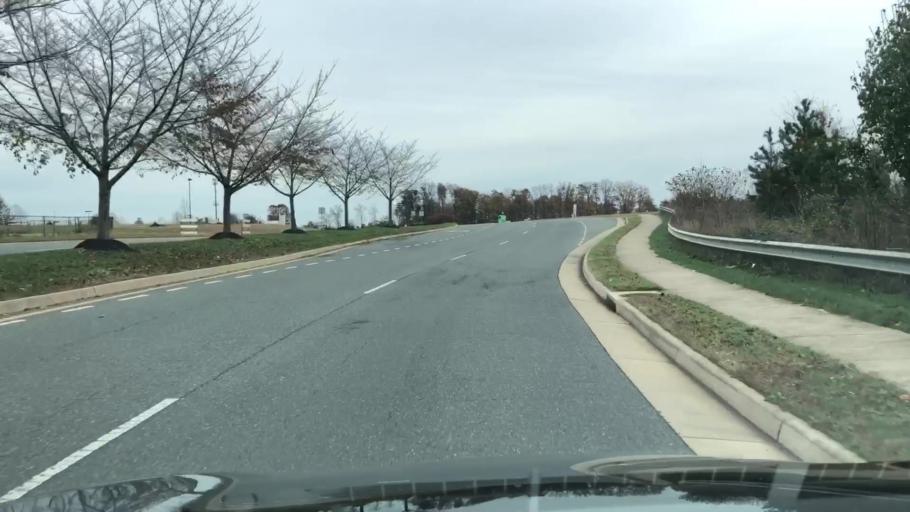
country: US
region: Virginia
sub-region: Stafford County
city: Falmouth
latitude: 38.3551
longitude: -77.5208
